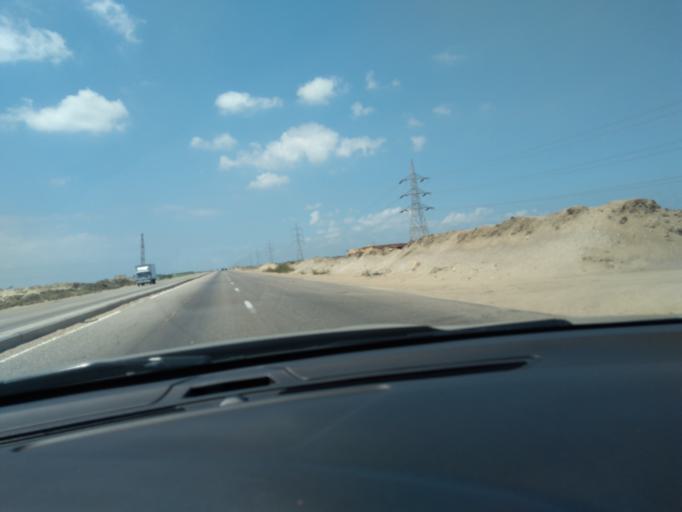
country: EG
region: Muhafazat Bur Sa`id
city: Port Said
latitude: 31.3081
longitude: 32.1347
